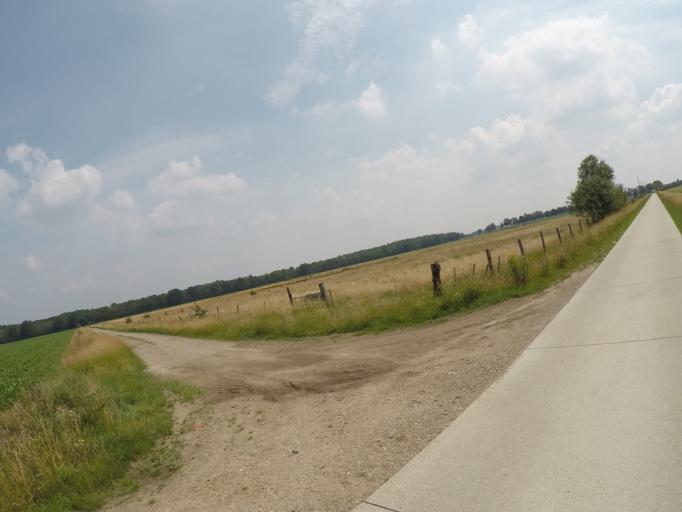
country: BE
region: Flanders
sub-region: Provincie Antwerpen
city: Rijkevorsel
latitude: 51.3657
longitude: 4.7243
